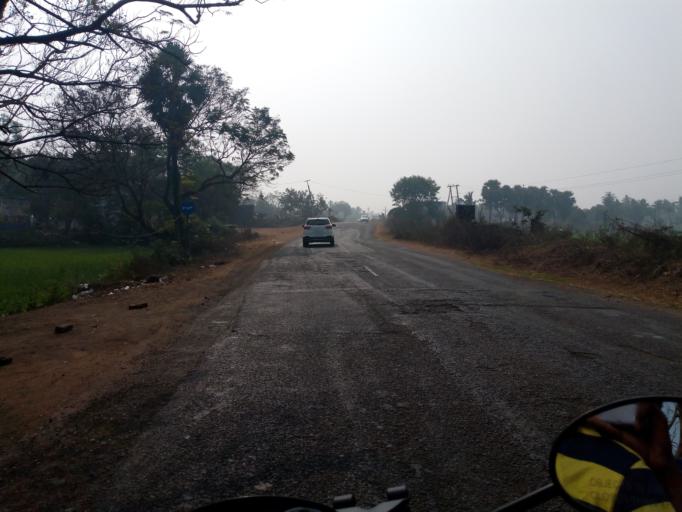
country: IN
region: Andhra Pradesh
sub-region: West Godavari
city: Tadepallegudem
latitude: 16.7988
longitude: 81.4139
